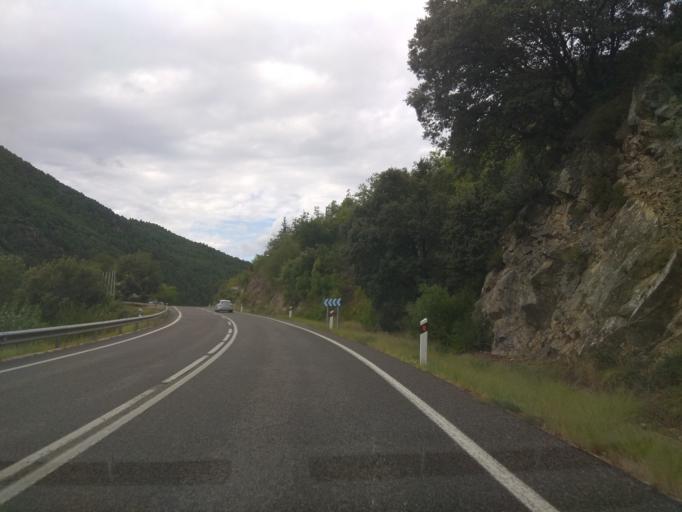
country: ES
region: Catalonia
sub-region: Provincia de Lleida
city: Alas i Cerc
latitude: 42.3595
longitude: 1.5580
